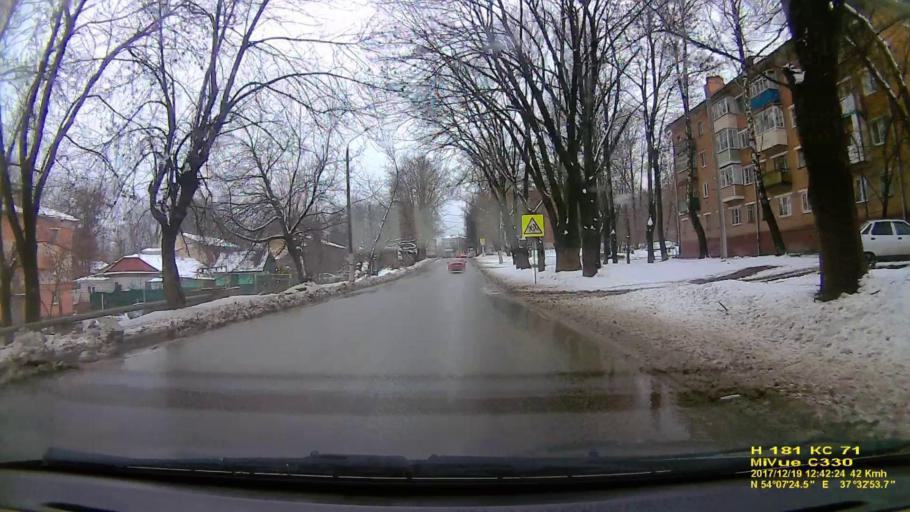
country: RU
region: Tula
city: Kosaya Gora
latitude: 54.1234
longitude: 37.5481
